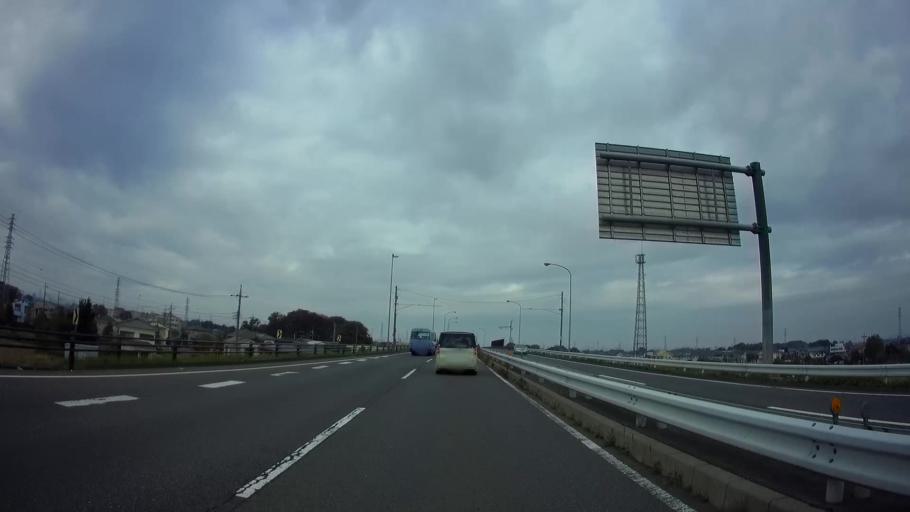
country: JP
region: Saitama
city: Kumagaya
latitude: 36.1691
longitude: 139.3784
